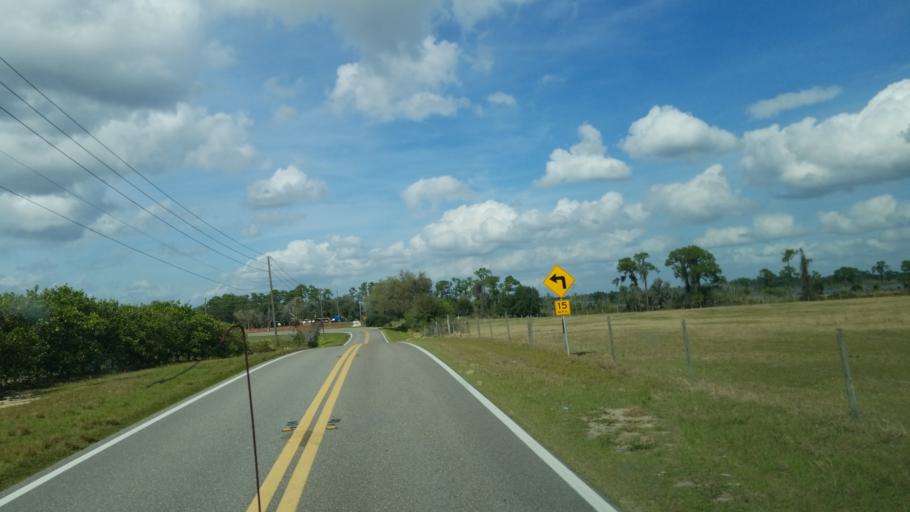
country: US
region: Florida
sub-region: Polk County
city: Lake Wales
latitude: 27.9232
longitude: -81.4966
